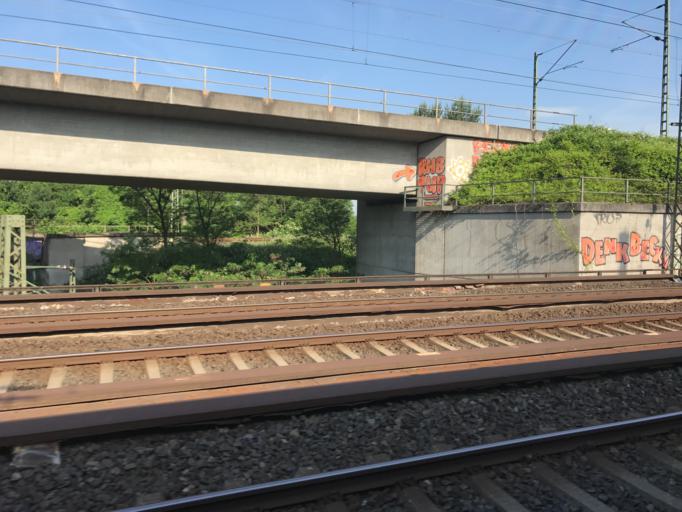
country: DE
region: Hesse
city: Niederrad
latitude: 50.0926
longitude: 8.6301
